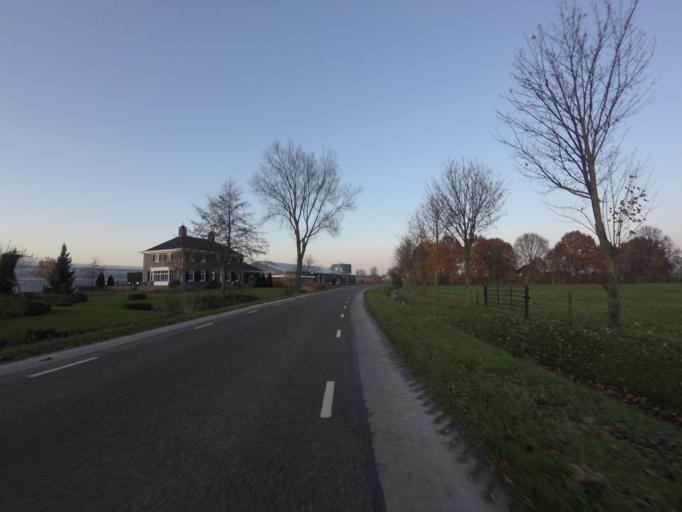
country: NL
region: Gelderland
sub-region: Gemeente Zaltbommel
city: Zaltbommel
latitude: 51.7764
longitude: 5.2371
